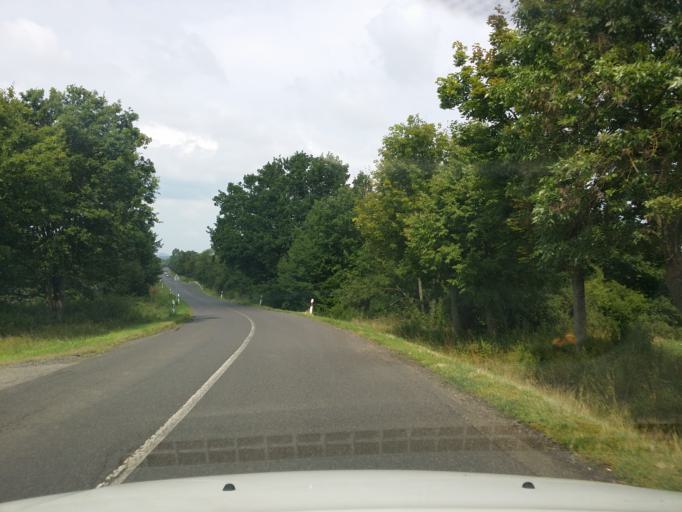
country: HU
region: Borsod-Abauj-Zemplen
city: Satoraljaujhely
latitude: 48.4705
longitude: 21.5701
